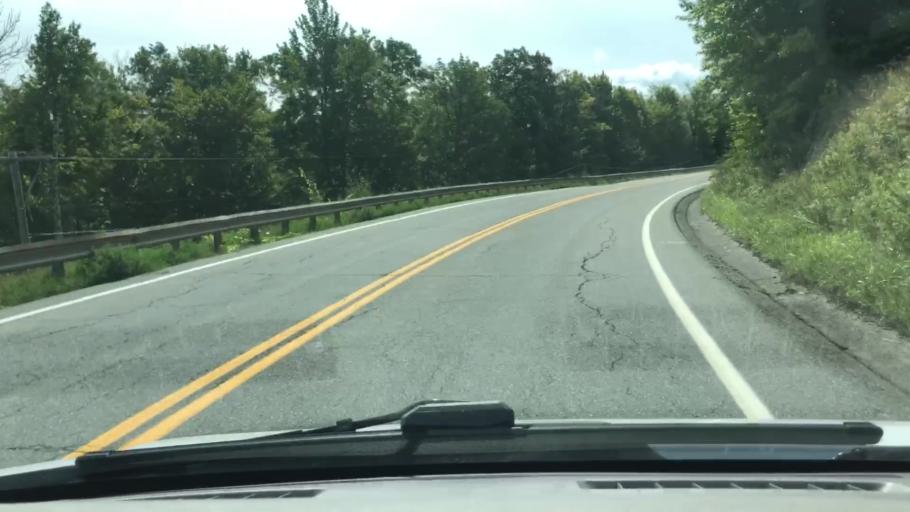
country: US
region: Massachusetts
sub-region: Berkshire County
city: North Adams
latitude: 42.6766
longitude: -73.0153
